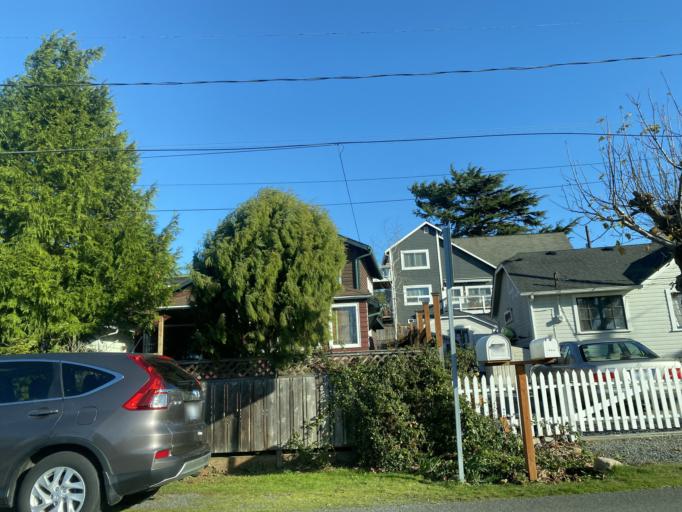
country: US
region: Washington
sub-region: Snohomish County
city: Woodway
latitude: 47.7721
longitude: -122.3922
